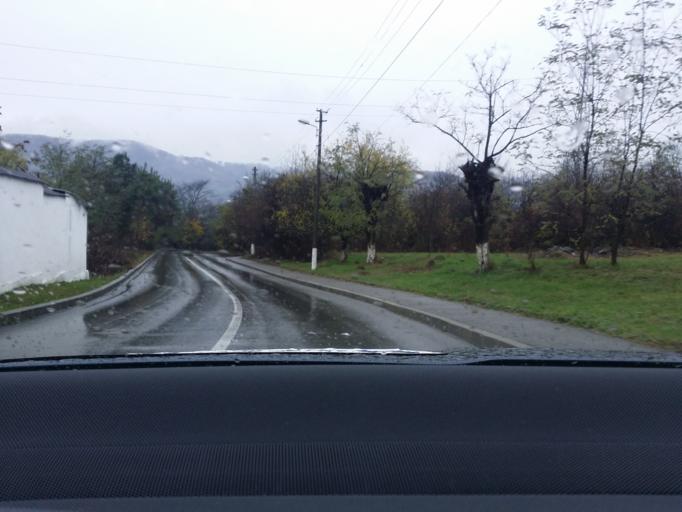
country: RO
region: Prahova
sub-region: Municipiul Campina
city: Campina
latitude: 45.1285
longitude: 25.7244
